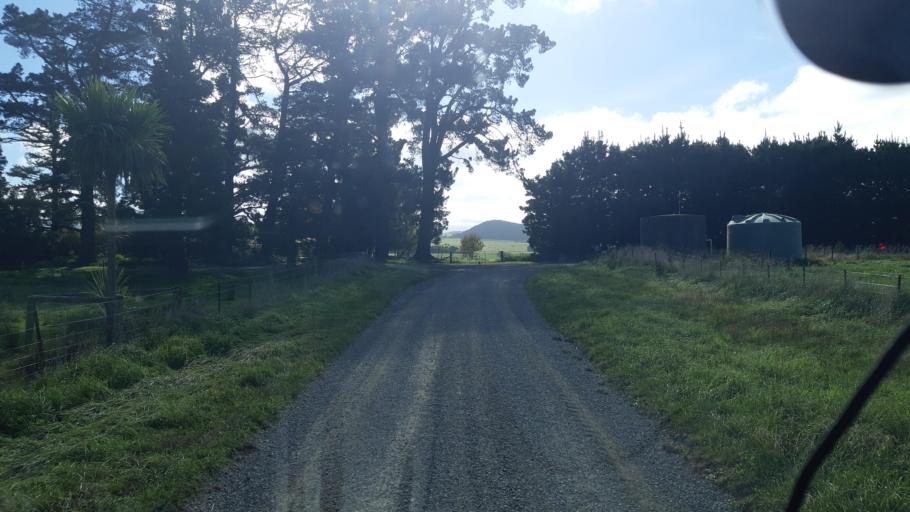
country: NZ
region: Canterbury
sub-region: Waimakariri District
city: Oxford
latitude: -43.2113
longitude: 172.4025
